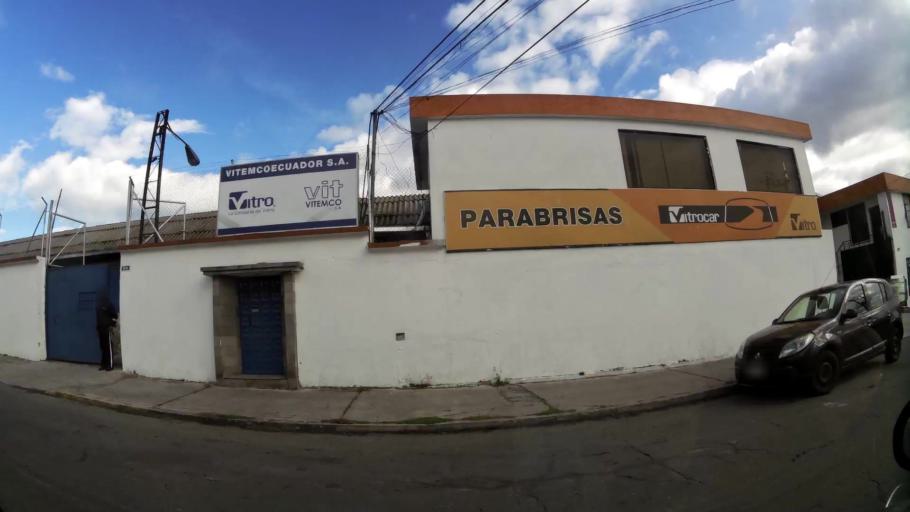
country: EC
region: Pichincha
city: Quito
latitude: -0.1366
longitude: -78.4725
